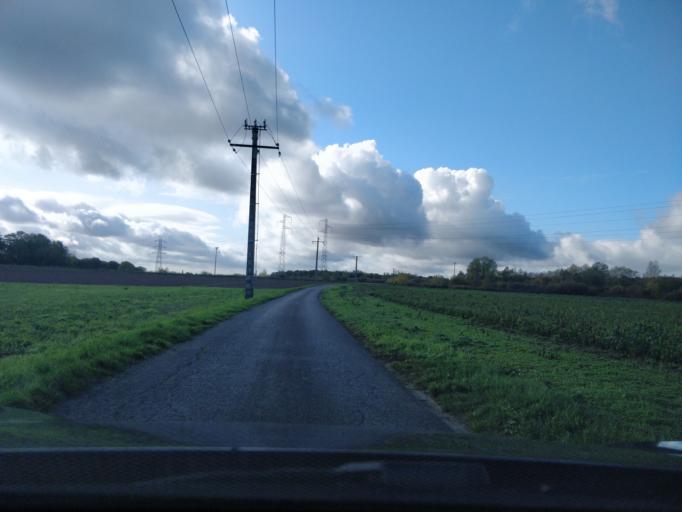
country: FR
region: Ile-de-France
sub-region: Departement de l'Essonne
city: Fontenay-les-Briis
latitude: 48.6299
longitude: 2.1469
